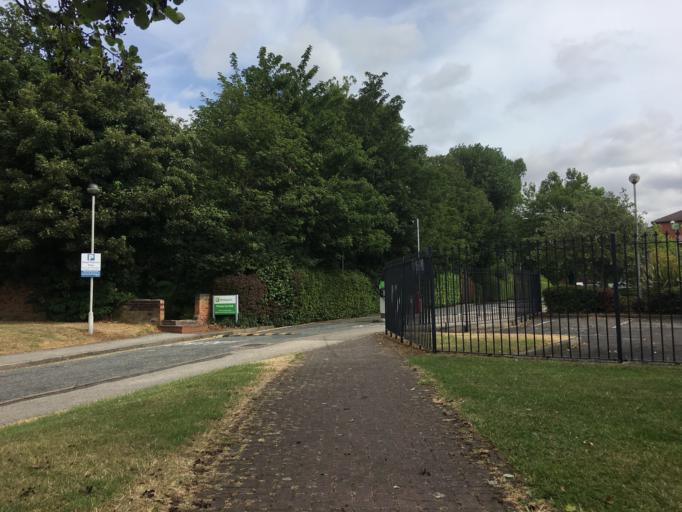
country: GB
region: England
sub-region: City of Kingston upon Hull
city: Hull
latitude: 53.7396
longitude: -0.3428
